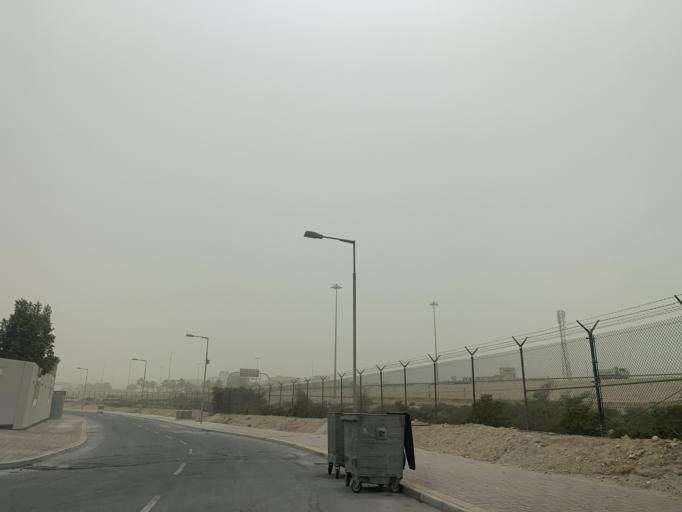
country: BH
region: Central Governorate
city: Madinat Hamad
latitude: 26.1379
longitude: 50.5120
